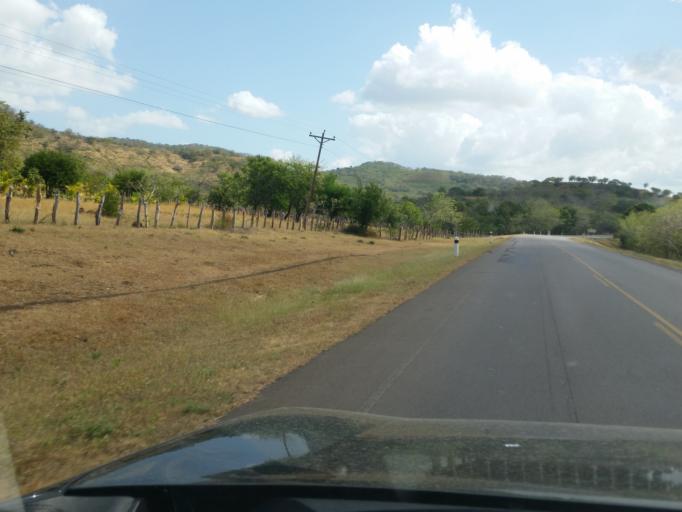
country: NI
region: Chontales
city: Comalapa
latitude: 12.2239
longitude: -85.6412
